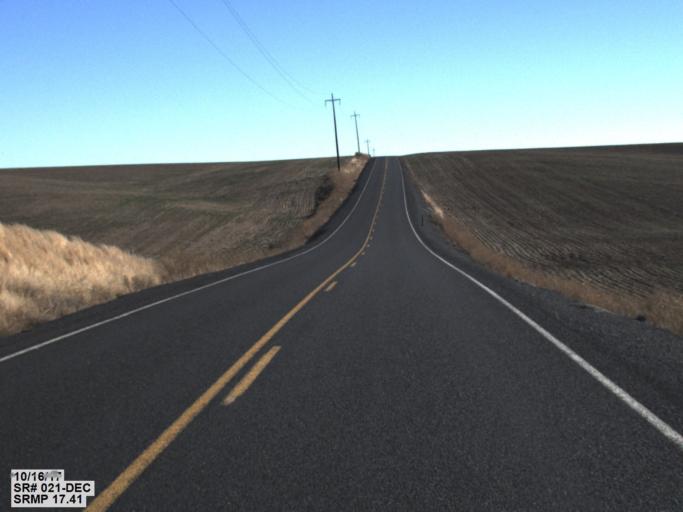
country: US
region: Washington
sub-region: Adams County
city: Ritzville
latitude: 46.8756
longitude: -118.5560
